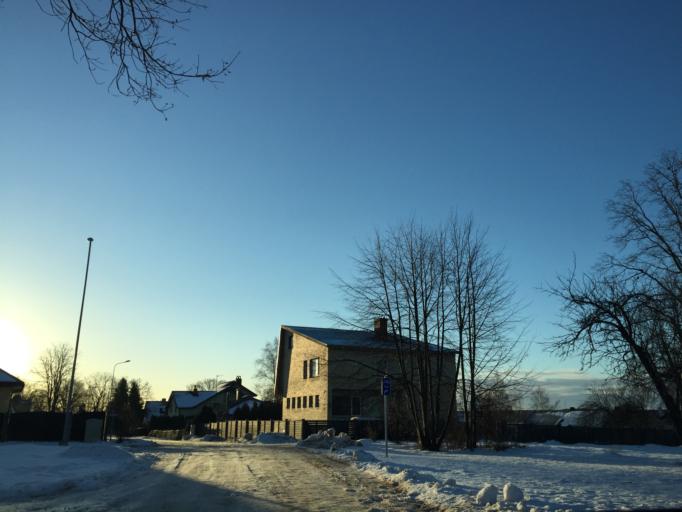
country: LV
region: Kegums
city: Kegums
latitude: 56.7402
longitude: 24.7229
